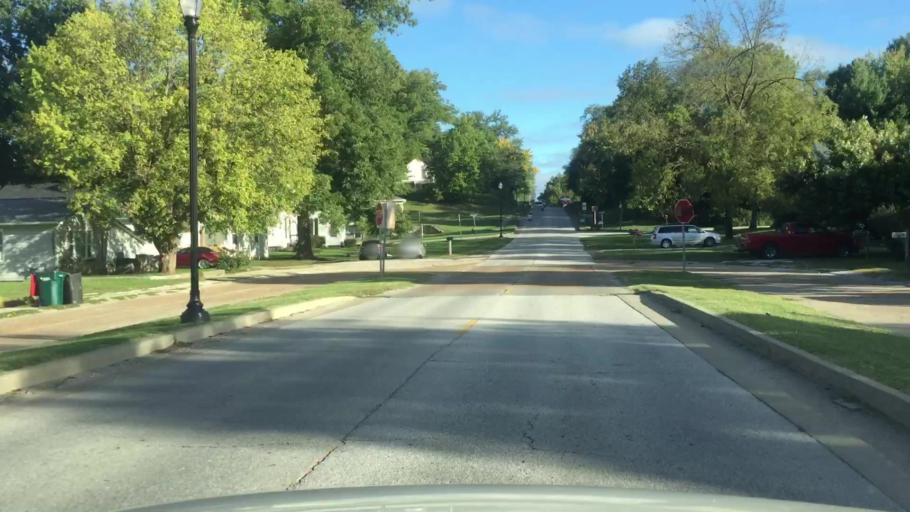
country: US
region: Missouri
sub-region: Howard County
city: New Franklin
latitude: 39.0143
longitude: -92.7376
